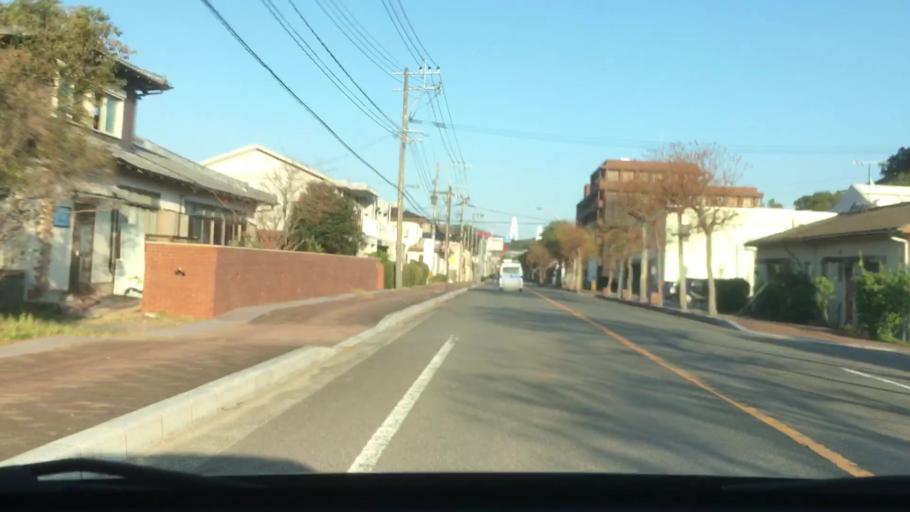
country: JP
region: Nagasaki
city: Sasebo
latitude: 33.0351
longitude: 129.6174
